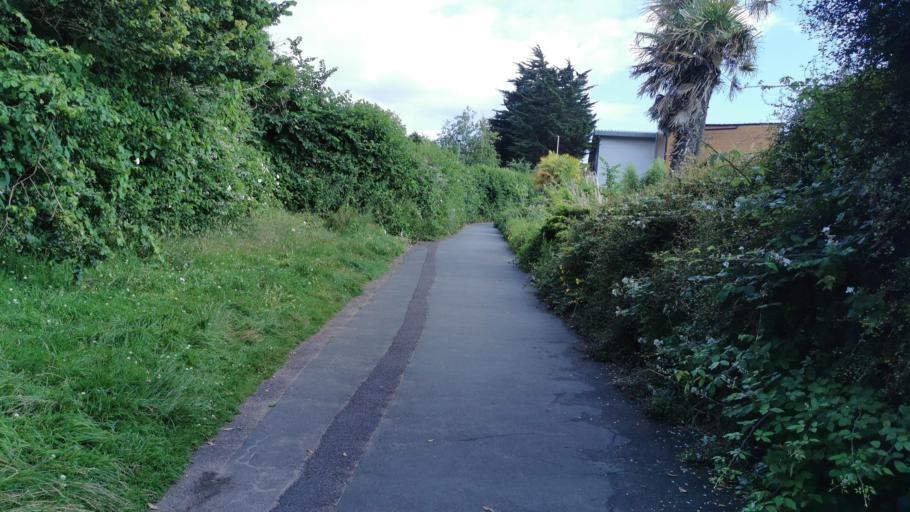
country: GB
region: England
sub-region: Devon
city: Exmouth
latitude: 50.6148
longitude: -3.4110
